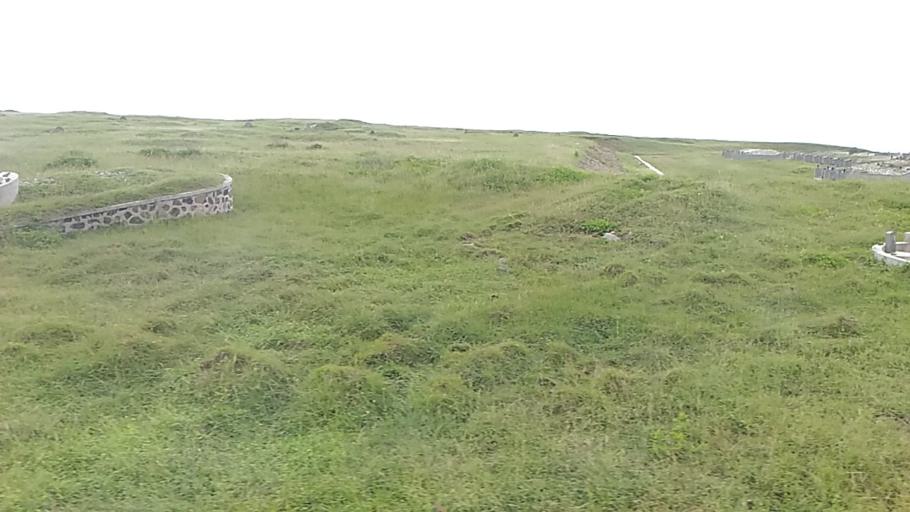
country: TW
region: Taiwan
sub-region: Penghu
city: Ma-kung
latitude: 23.2198
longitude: 119.4413
